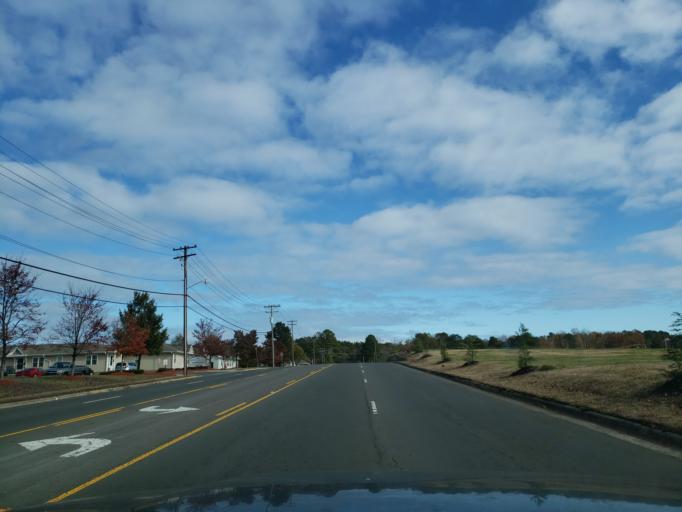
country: US
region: North Carolina
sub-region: Durham County
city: Durham
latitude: 35.9605
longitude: -78.9135
